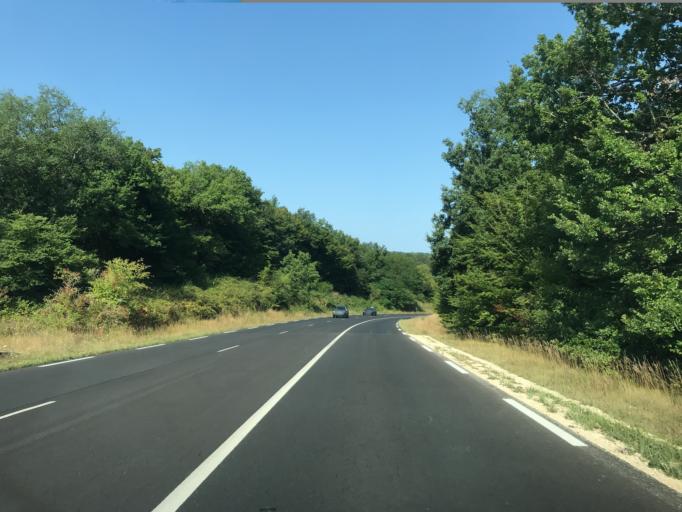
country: FR
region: Aquitaine
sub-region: Departement de la Dordogne
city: Montignac
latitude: 45.0487
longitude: 1.2165
